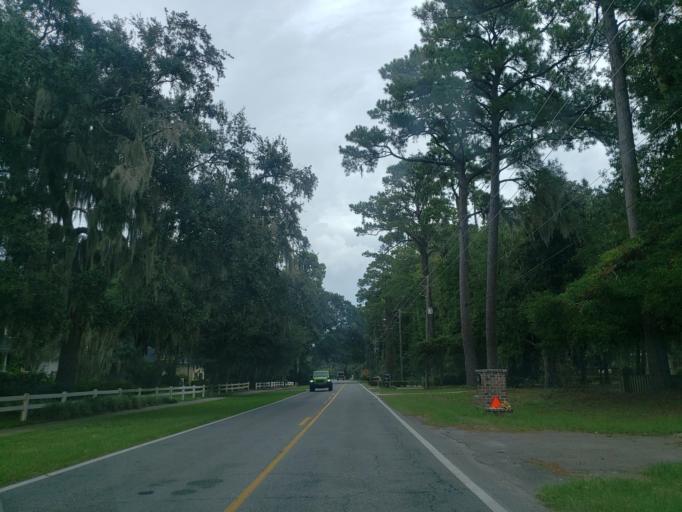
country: US
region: Georgia
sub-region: Chatham County
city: Wilmington Island
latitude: 31.9995
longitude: -80.9707
